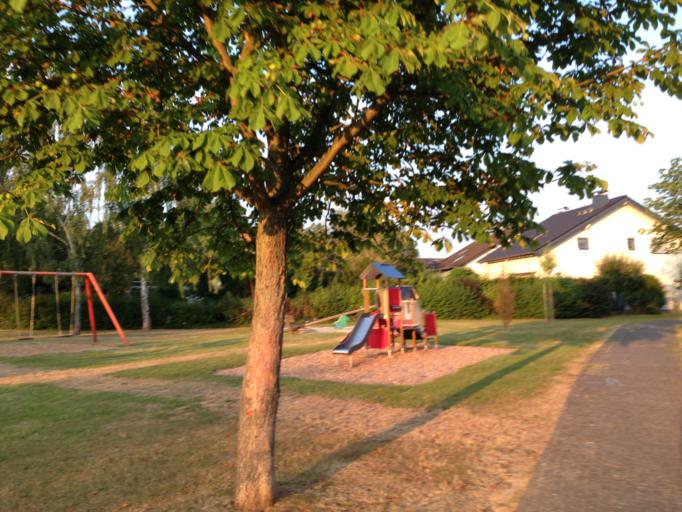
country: DE
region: Hesse
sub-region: Regierungsbezirk Giessen
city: Langgons
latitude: 50.5224
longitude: 8.6572
